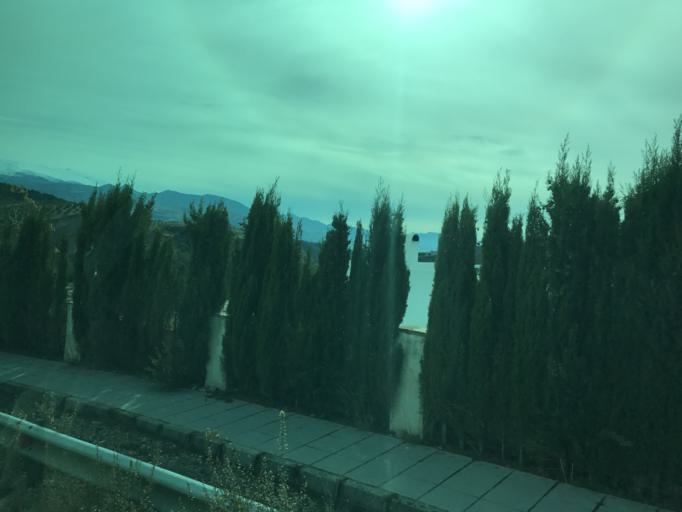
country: ES
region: Andalusia
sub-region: Provincia de Granada
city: Huetor Santillan
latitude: 37.2165
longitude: -3.5214
